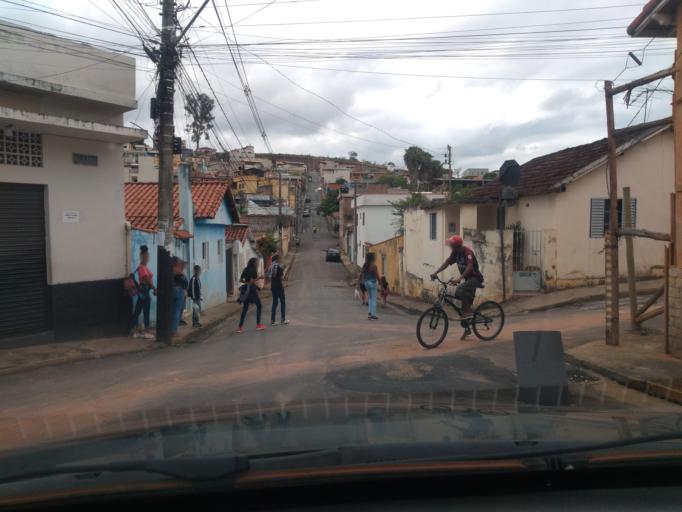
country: BR
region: Minas Gerais
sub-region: Tres Coracoes
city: Tres Coracoes
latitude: -21.6922
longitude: -45.2558
